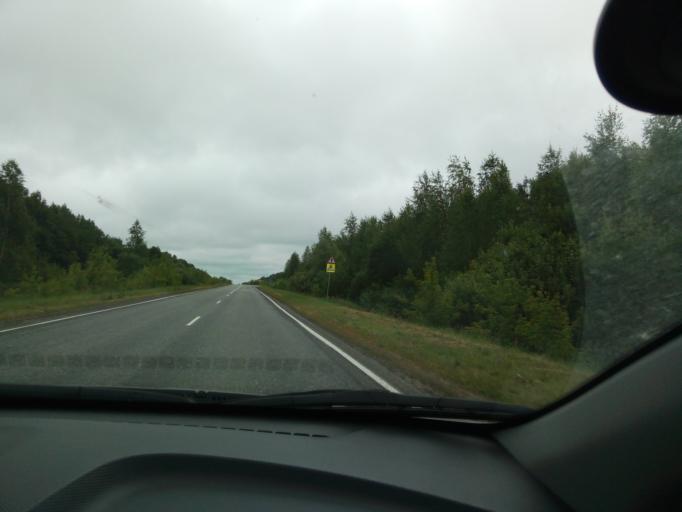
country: RU
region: Chuvashia
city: Alikovo
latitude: 55.6115
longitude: 46.6600
